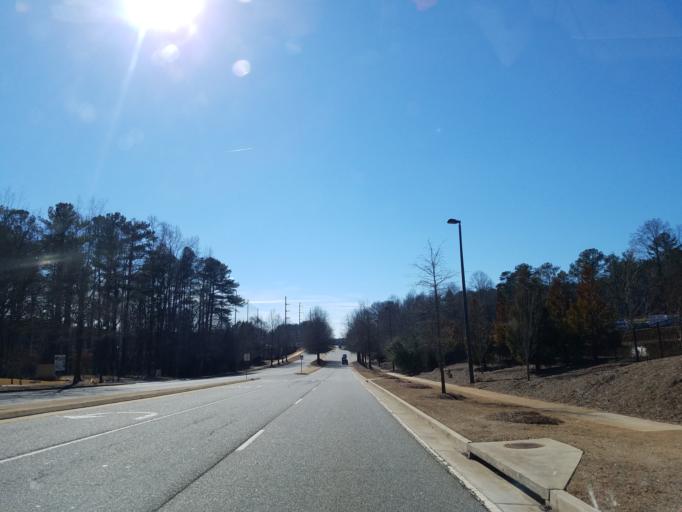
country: US
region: Georgia
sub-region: Fulton County
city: Alpharetta
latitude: 34.0478
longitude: -84.3059
